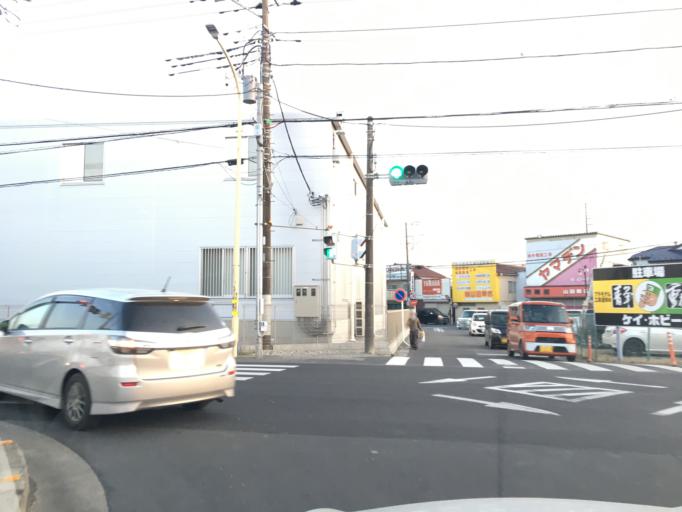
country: JP
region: Saitama
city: Kawagoe
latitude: 35.9190
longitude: 139.4590
